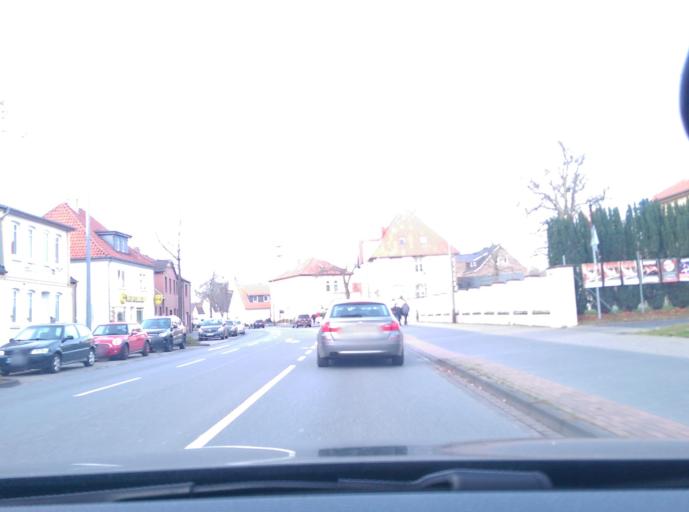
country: DE
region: Lower Saxony
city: Celle
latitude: 52.6148
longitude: 10.0791
